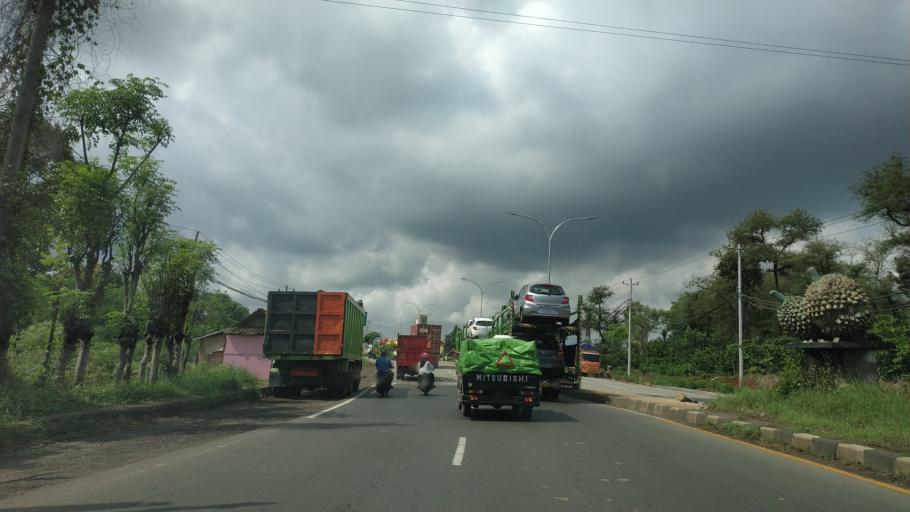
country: ID
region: Central Java
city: Pekalongan
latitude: -6.9303
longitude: 109.7642
